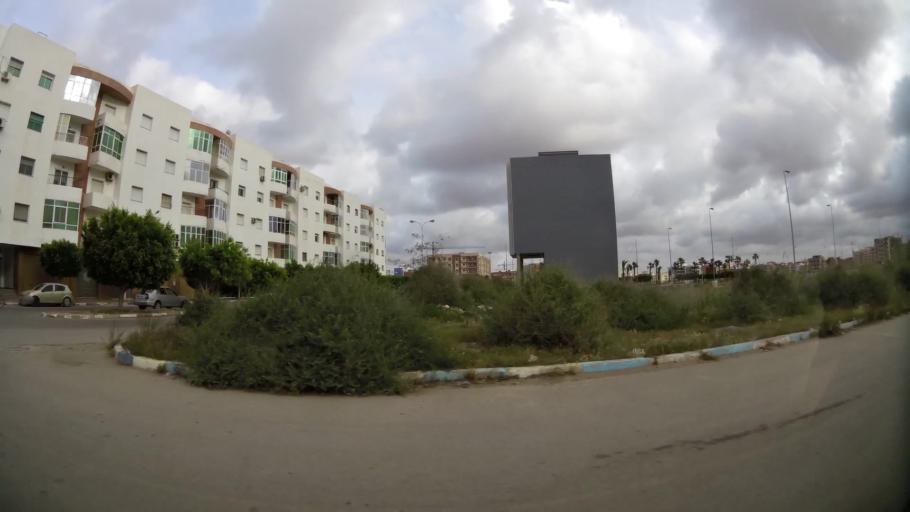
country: MA
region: Oriental
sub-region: Nador
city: Nador
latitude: 35.1548
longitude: -2.9120
